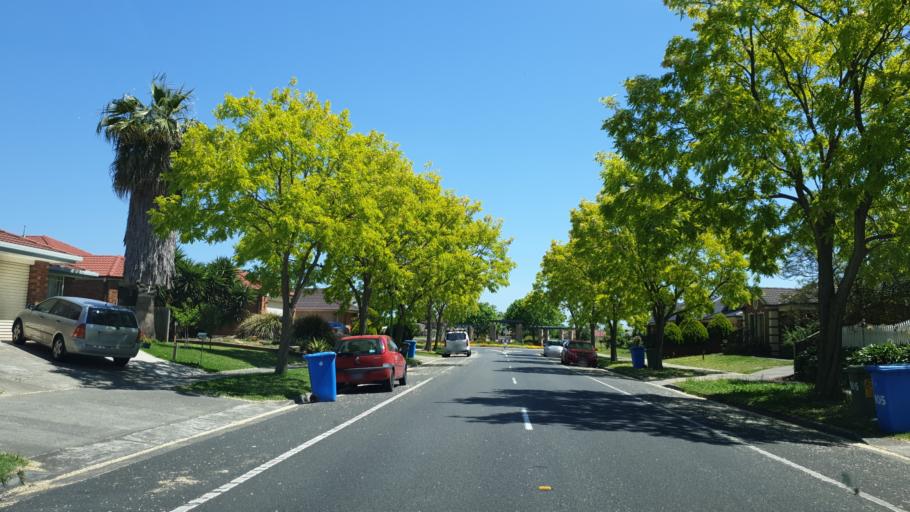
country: AU
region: Victoria
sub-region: Casey
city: Narre Warren South
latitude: -38.0607
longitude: 145.2868
